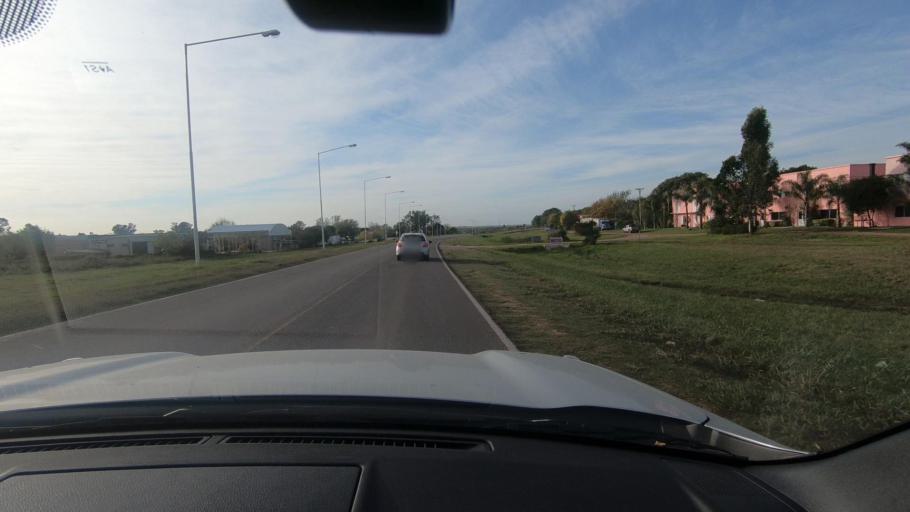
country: AR
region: Entre Rios
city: Colon
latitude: -32.2587
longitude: -58.2323
